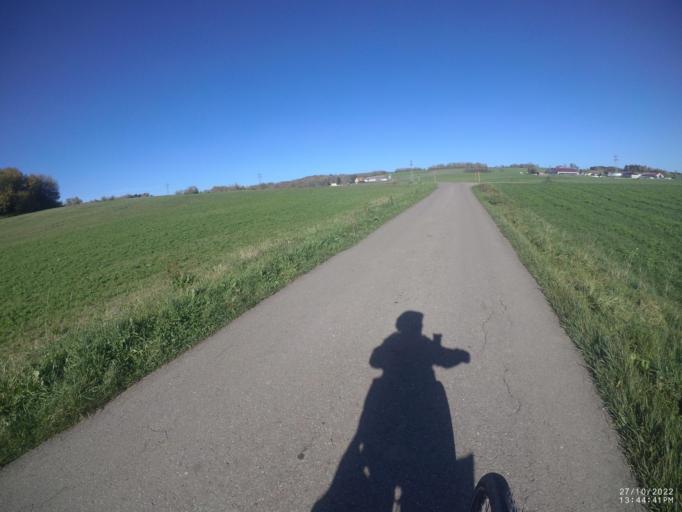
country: DE
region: Baden-Wuerttemberg
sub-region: Regierungsbezirk Stuttgart
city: Hohenstadt
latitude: 48.5558
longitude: 9.6953
